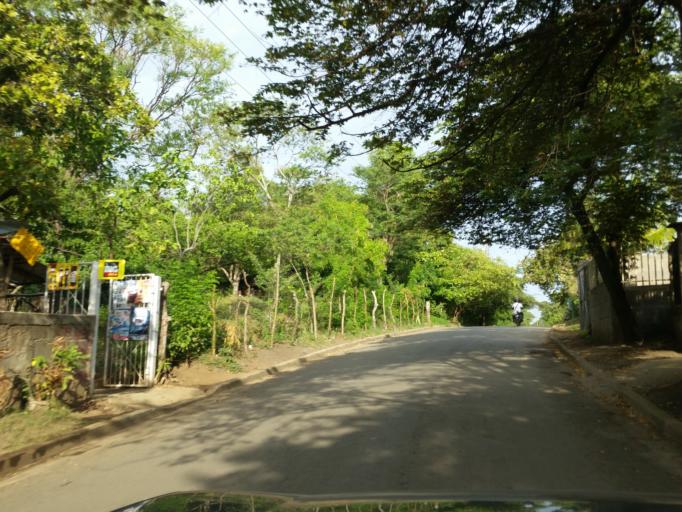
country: NI
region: Managua
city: Managua
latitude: 12.1066
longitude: -86.2187
